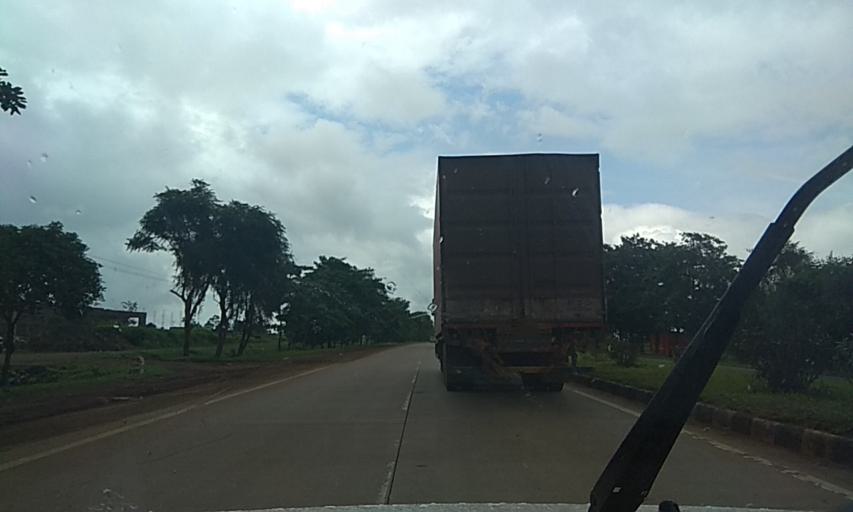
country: IN
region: Karnataka
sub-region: Belgaum
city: Sankeshwar
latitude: 16.2977
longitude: 74.4362
